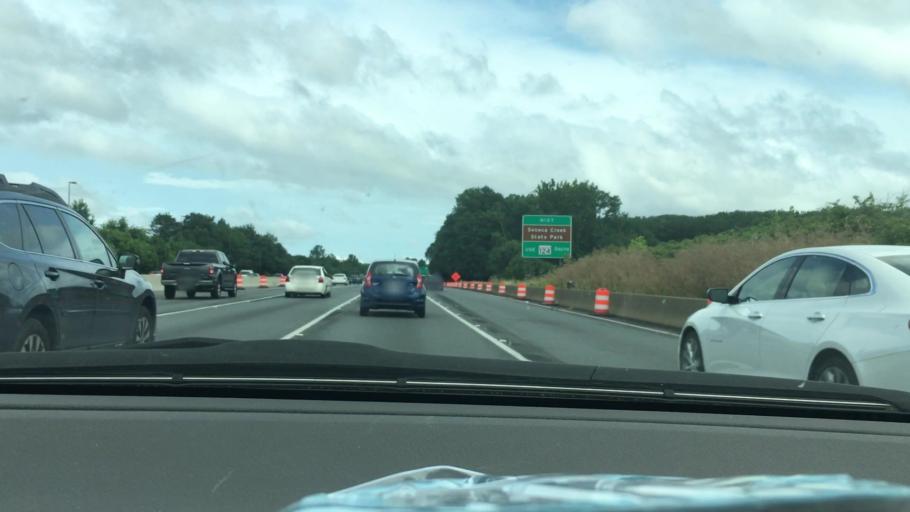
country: US
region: Maryland
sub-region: Montgomery County
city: Gaithersburg
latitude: 39.1554
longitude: -77.2245
